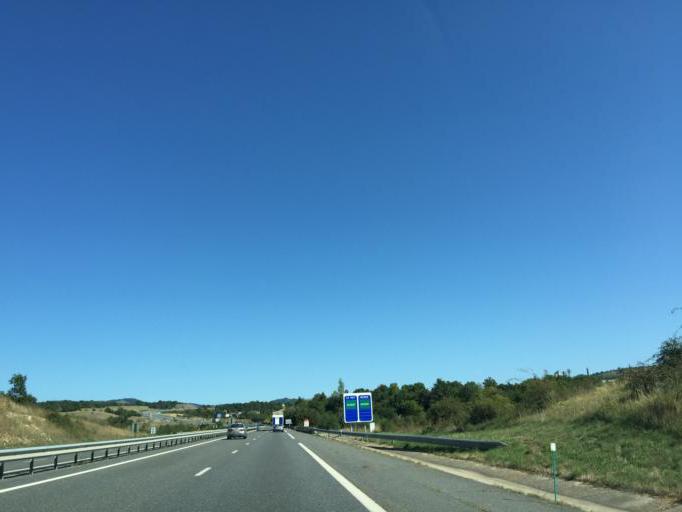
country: FR
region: Midi-Pyrenees
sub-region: Departement de l'Aveyron
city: Severac-le-Chateau
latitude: 44.3346
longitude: 3.0580
